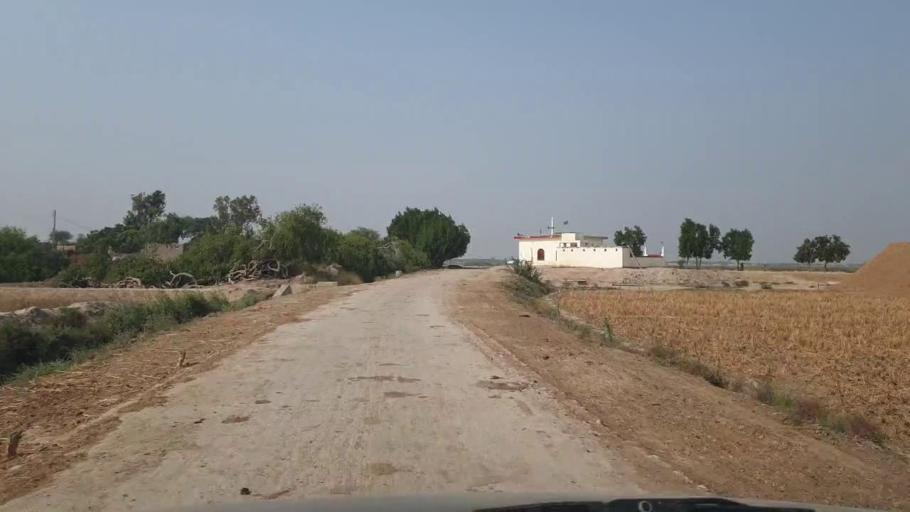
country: PK
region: Sindh
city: Bulri
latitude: 25.0340
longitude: 68.3825
